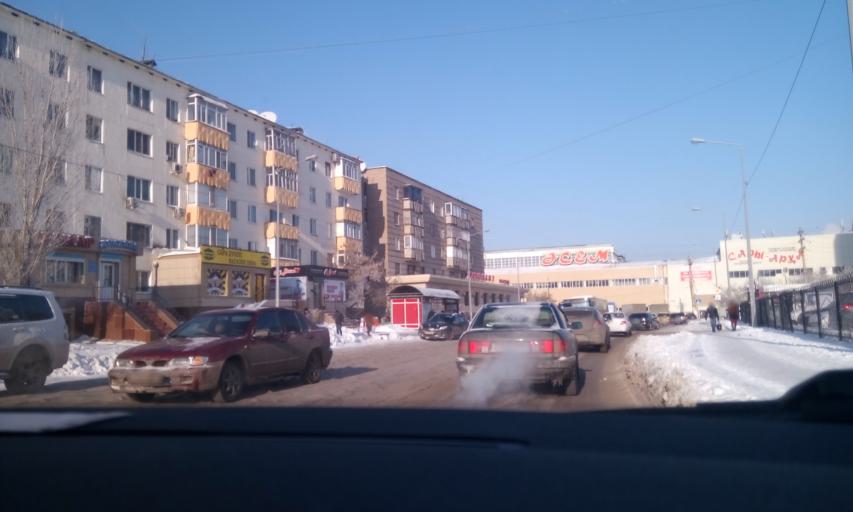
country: KZ
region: Astana Qalasy
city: Astana
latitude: 51.1797
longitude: 71.4359
